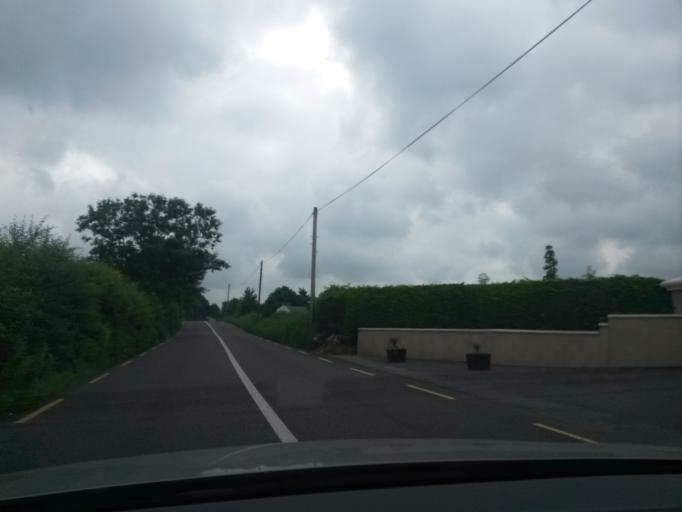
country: IE
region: Munster
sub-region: Ciarrai
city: Tralee
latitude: 52.1629
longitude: -9.6944
